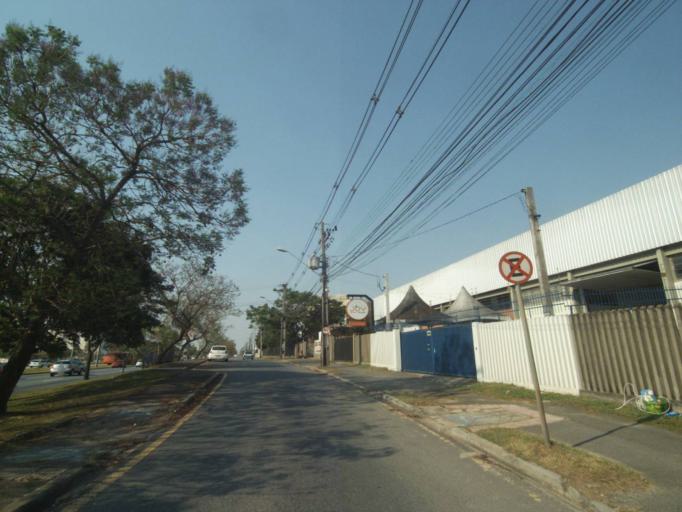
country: BR
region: Parana
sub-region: Curitiba
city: Curitiba
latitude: -25.4953
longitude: -49.2746
